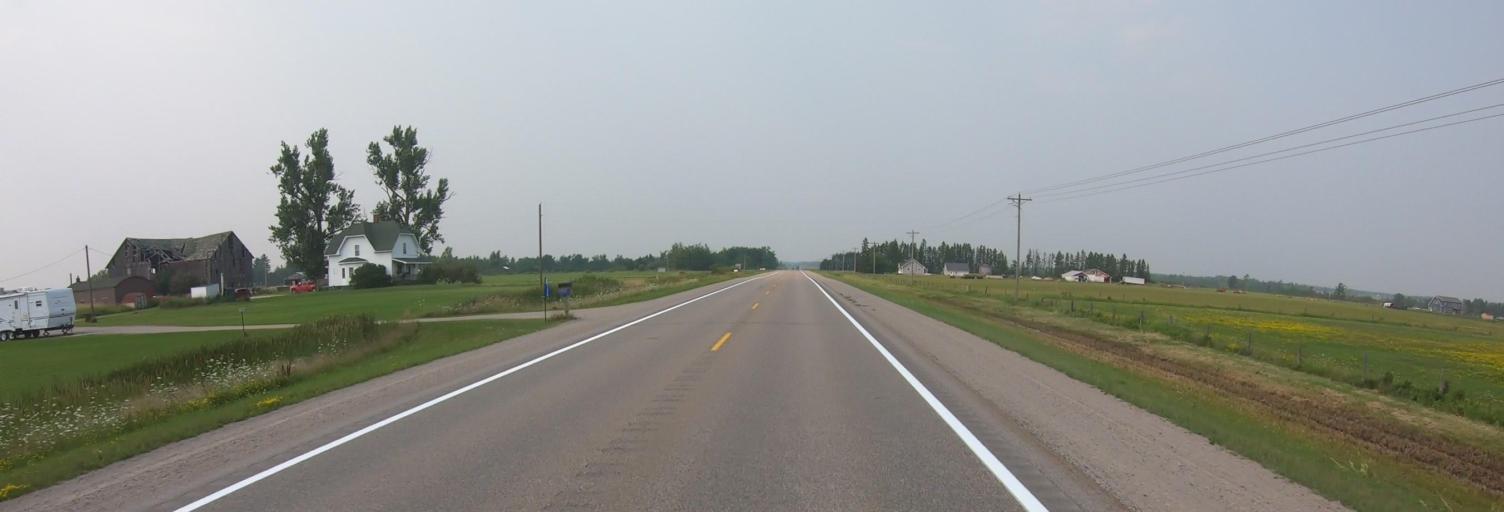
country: US
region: Michigan
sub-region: Chippewa County
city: Sault Ste. Marie
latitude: 46.3431
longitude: -84.3639
